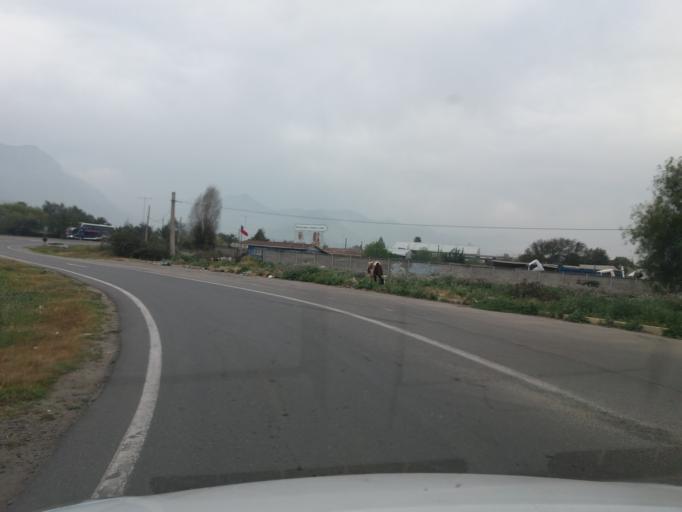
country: CL
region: Valparaiso
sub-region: Provincia de Quillota
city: Hacienda La Calera
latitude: -32.7725
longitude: -71.1888
